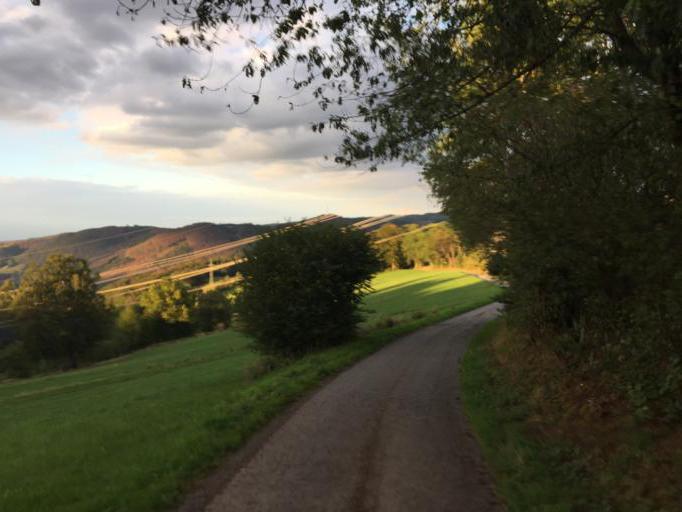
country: DE
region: North Rhine-Westphalia
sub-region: Regierungsbezirk Arnsberg
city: Nachrodt-Wiblingwerde
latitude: 51.3015
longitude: 7.6328
